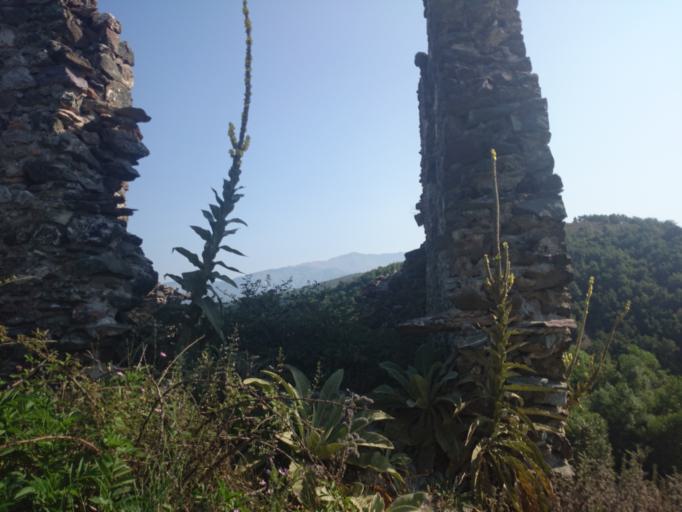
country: AL
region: Diber
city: Peshkopi
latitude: 41.6413
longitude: 20.4022
